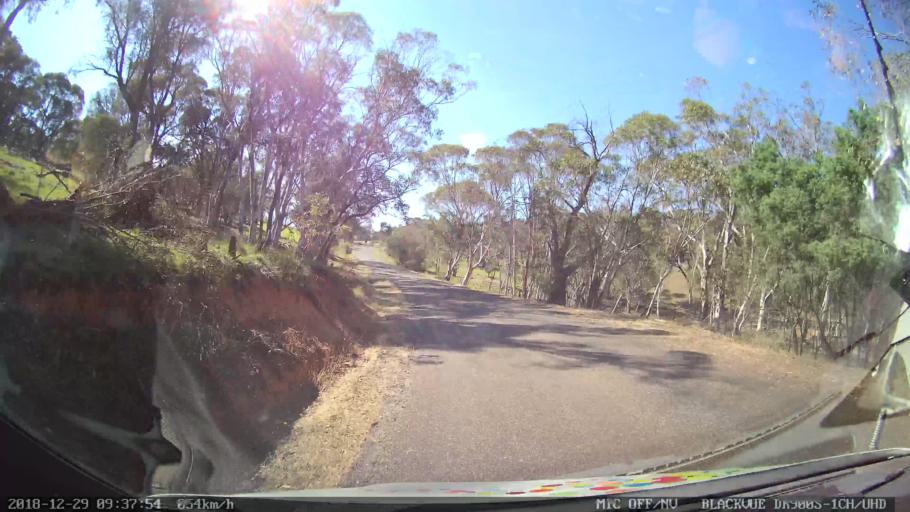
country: AU
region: New South Wales
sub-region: Upper Lachlan Shire
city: Crookwell
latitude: -34.6419
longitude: 149.3743
